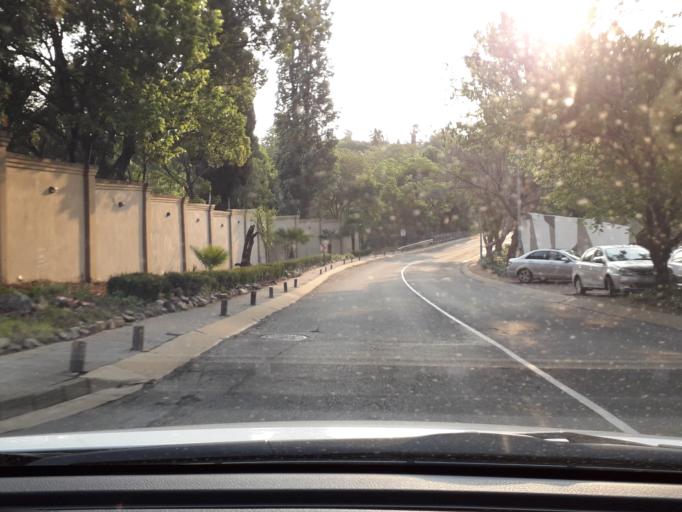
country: ZA
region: Gauteng
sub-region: City of Johannesburg Metropolitan Municipality
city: Modderfontein
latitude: -26.0738
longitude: 28.0709
